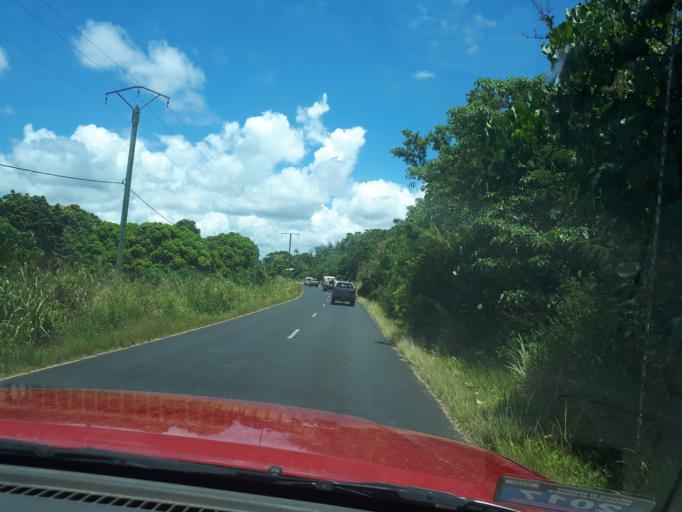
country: VU
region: Sanma
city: Luganville
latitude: -15.5157
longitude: 167.2076
